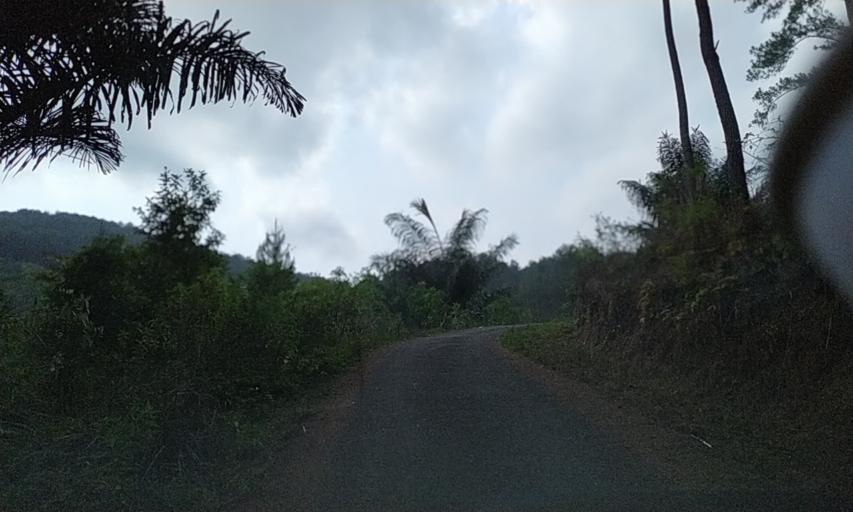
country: ID
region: Central Java
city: Cigintung
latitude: -7.2406
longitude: 108.7007
